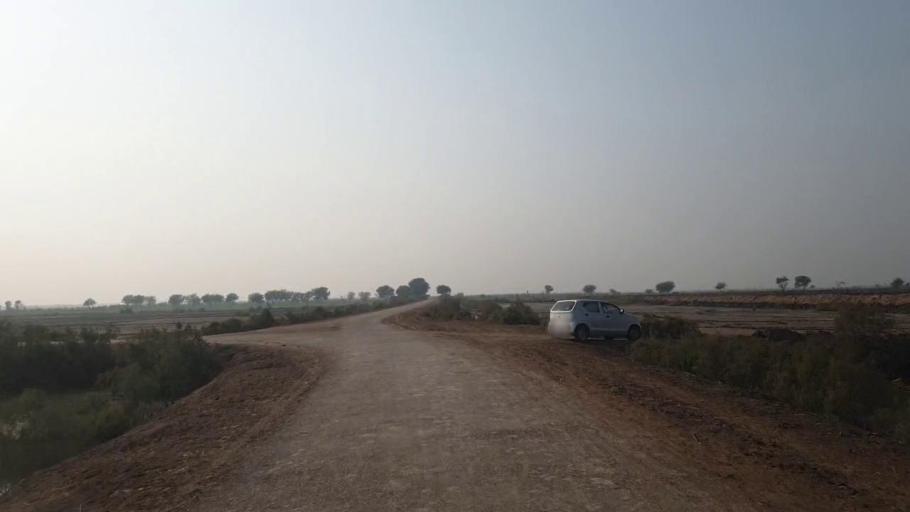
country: PK
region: Sindh
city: Shahdadpur
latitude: 25.9714
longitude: 68.5225
